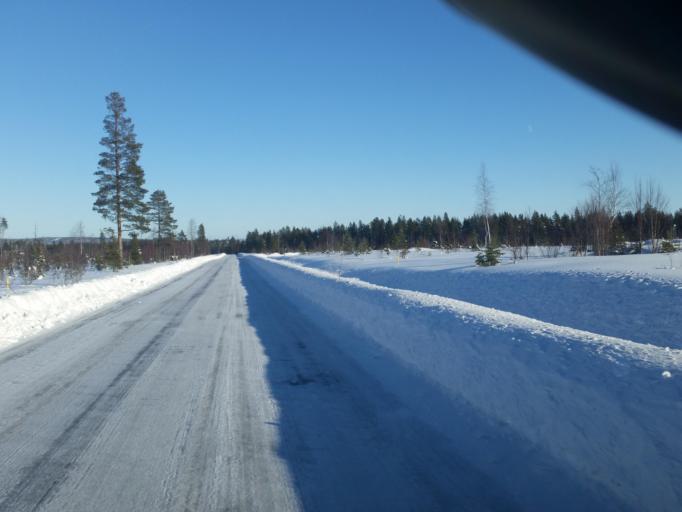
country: SE
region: Norrbotten
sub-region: Pitea Kommun
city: Roknas
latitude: 65.3459
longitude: 21.0080
